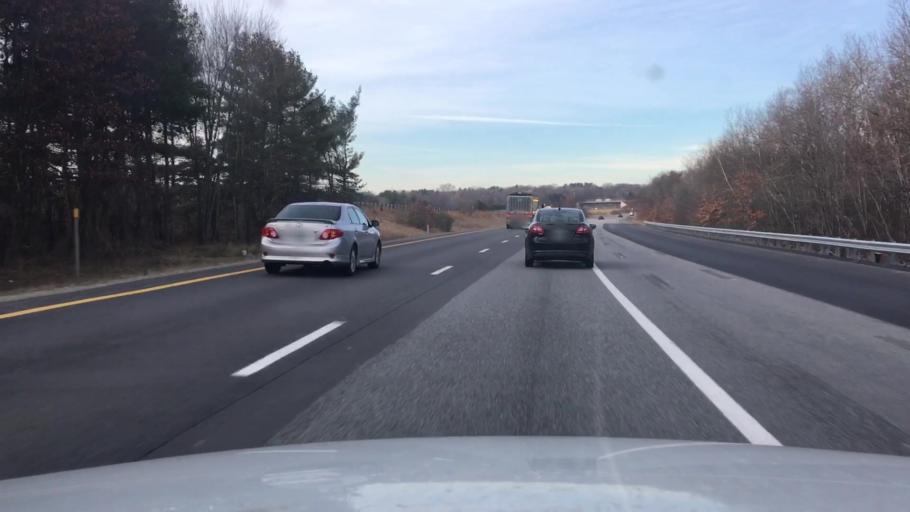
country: US
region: New Hampshire
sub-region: Hillsborough County
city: Manchester
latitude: 42.9618
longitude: -71.4094
